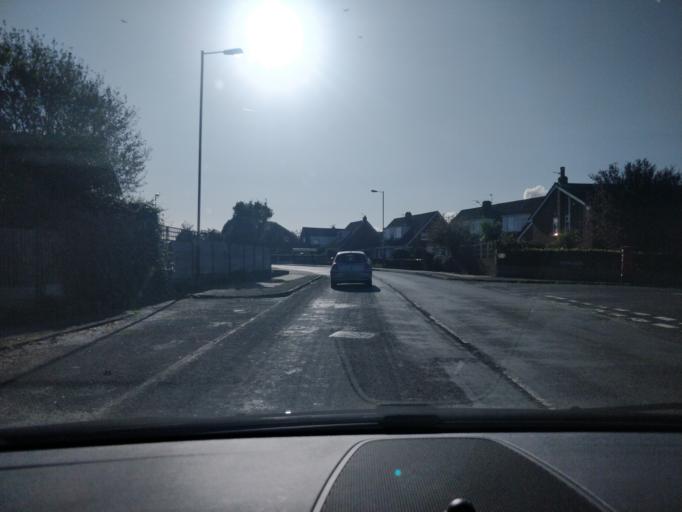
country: GB
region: England
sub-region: Lancashire
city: Banks
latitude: 53.6779
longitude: -2.9459
